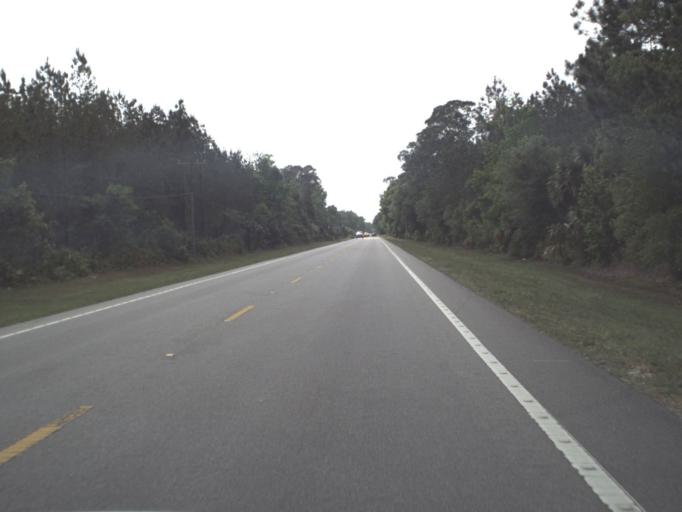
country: US
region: Florida
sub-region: Flagler County
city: Bunnell
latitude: 29.4672
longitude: -81.2947
